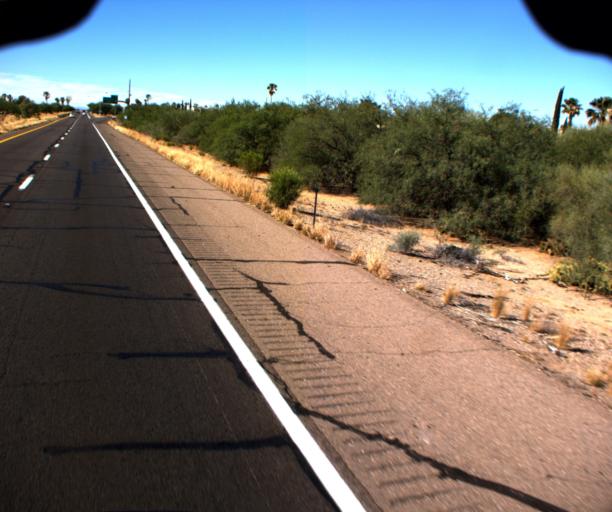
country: US
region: Arizona
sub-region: Pima County
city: Green Valley
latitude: 31.8753
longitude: -110.9898
